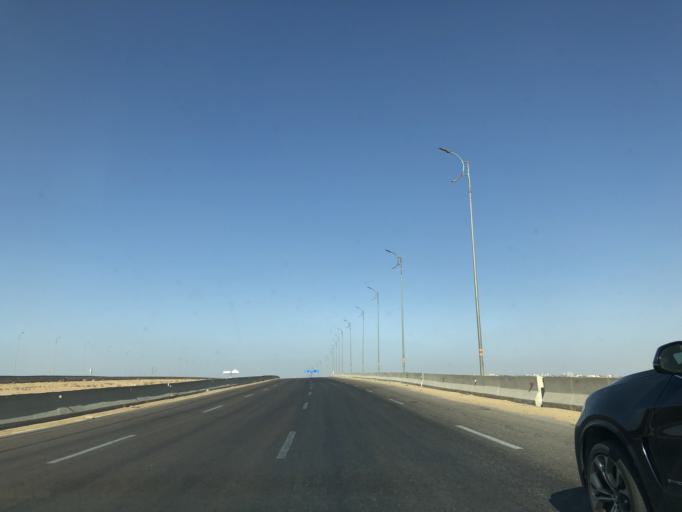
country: EG
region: Al Jizah
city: Awsim
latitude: 30.0724
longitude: 30.9174
